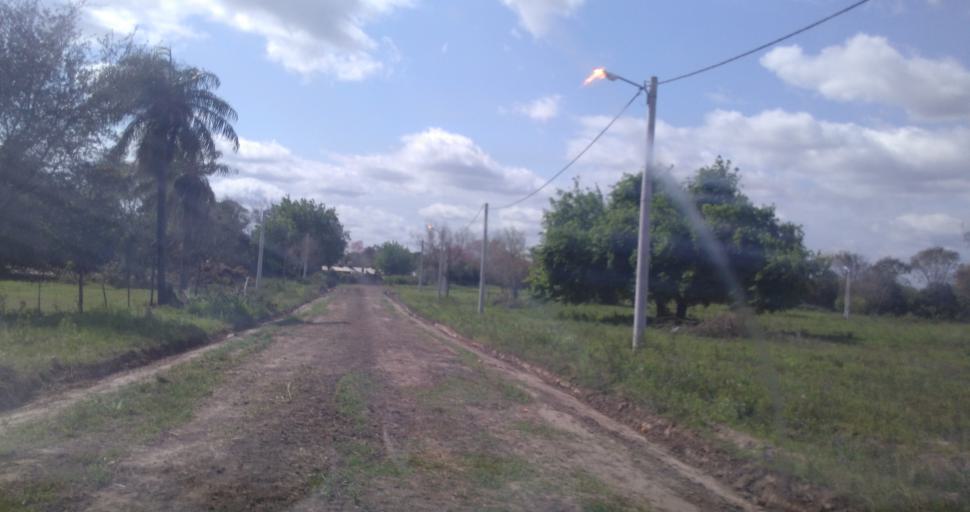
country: AR
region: Chaco
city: Fontana
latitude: -27.4280
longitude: -59.0245
